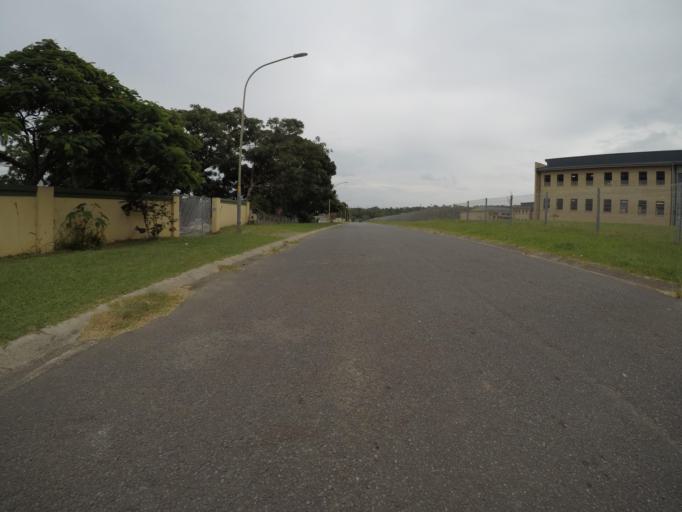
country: ZA
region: Eastern Cape
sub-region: Buffalo City Metropolitan Municipality
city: East London
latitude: -33.0005
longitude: 27.8582
